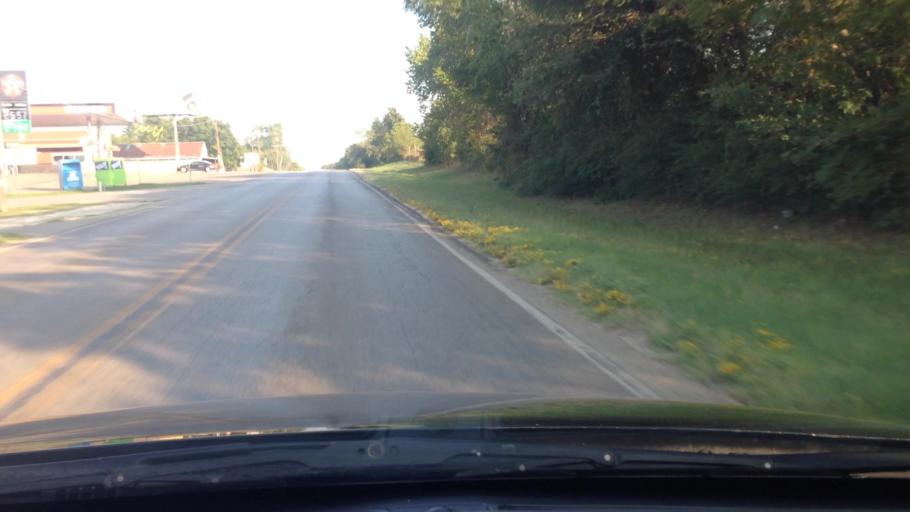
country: US
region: Texas
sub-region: Tarrant County
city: Rendon
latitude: 32.5860
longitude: -97.2456
